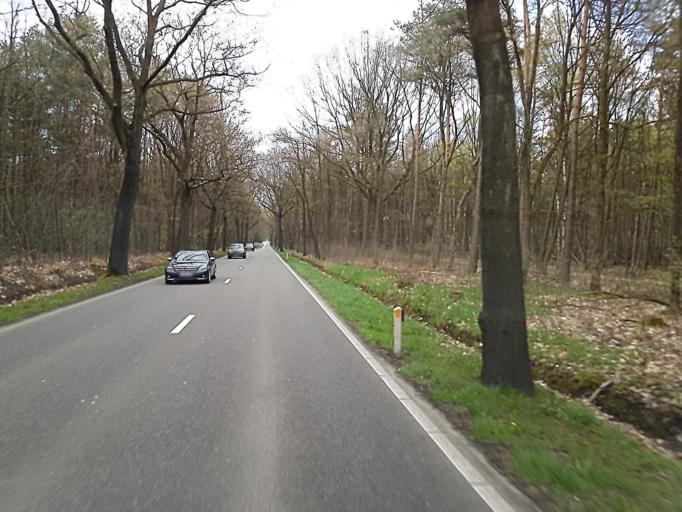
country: BE
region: Flanders
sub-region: Provincie Limburg
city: Zutendaal
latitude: 50.9650
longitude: 5.5513
